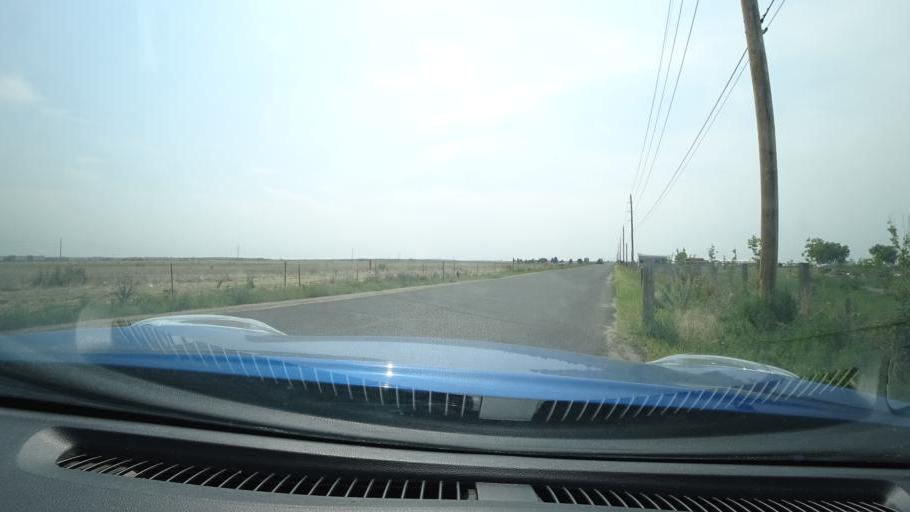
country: US
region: Colorado
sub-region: Adams County
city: Aurora
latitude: 39.7547
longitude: -104.7071
